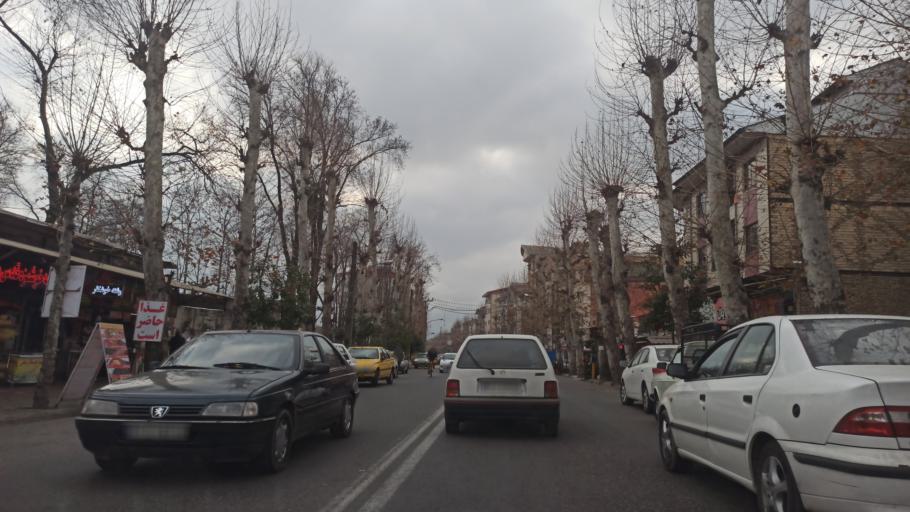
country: IR
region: Gilan
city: Fuman
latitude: 37.2319
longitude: 49.3182
